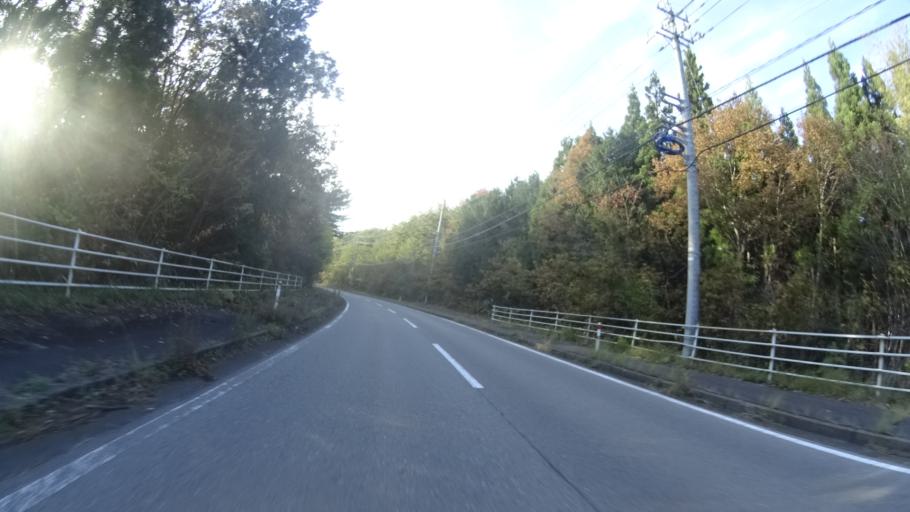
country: JP
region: Ishikawa
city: Hakui
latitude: 37.0670
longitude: 136.7648
